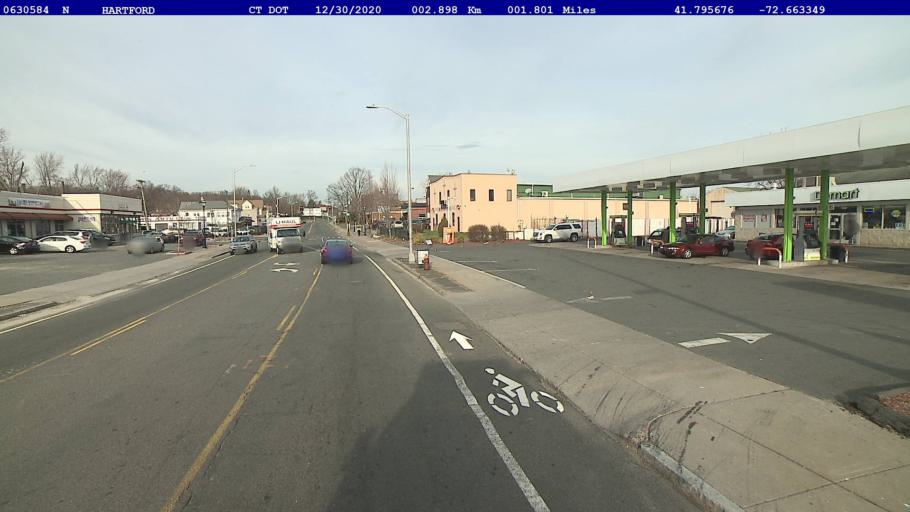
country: US
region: Connecticut
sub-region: Hartford County
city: Blue Hills
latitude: 41.7957
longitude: -72.6633
